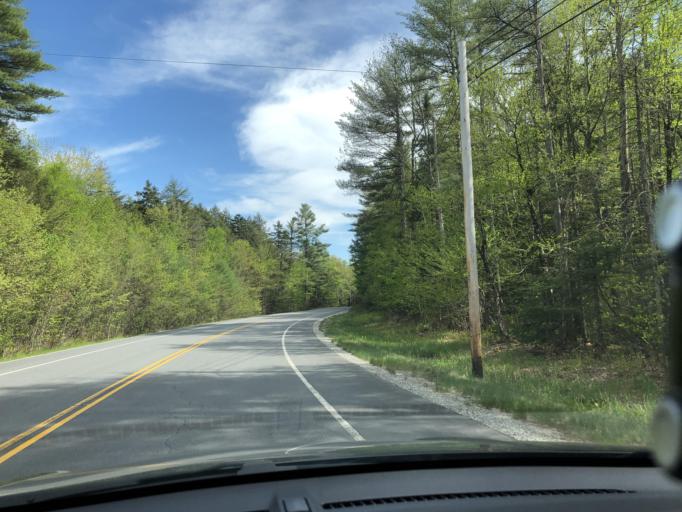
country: US
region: New Hampshire
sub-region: Merrimack County
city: New London
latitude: 43.4193
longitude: -72.0370
